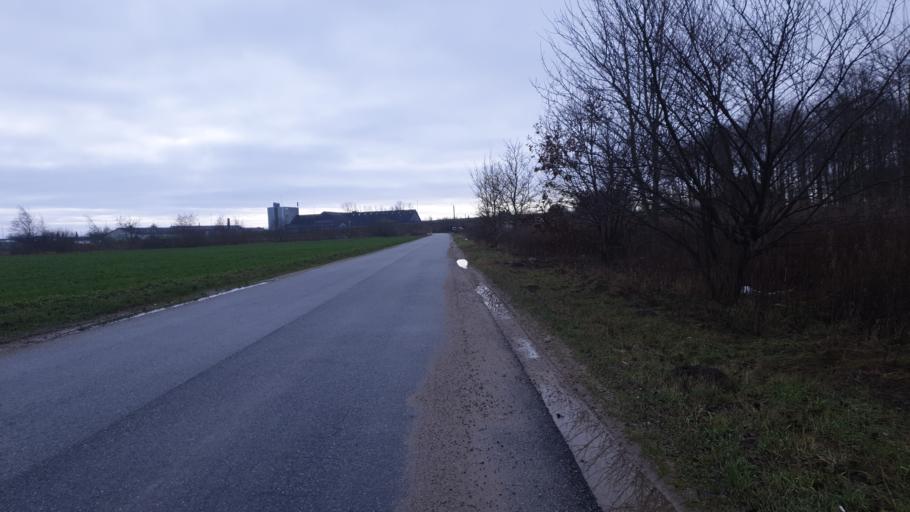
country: DK
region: Central Jutland
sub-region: Hedensted Kommune
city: Hedensted
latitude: 55.7838
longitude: 9.7001
